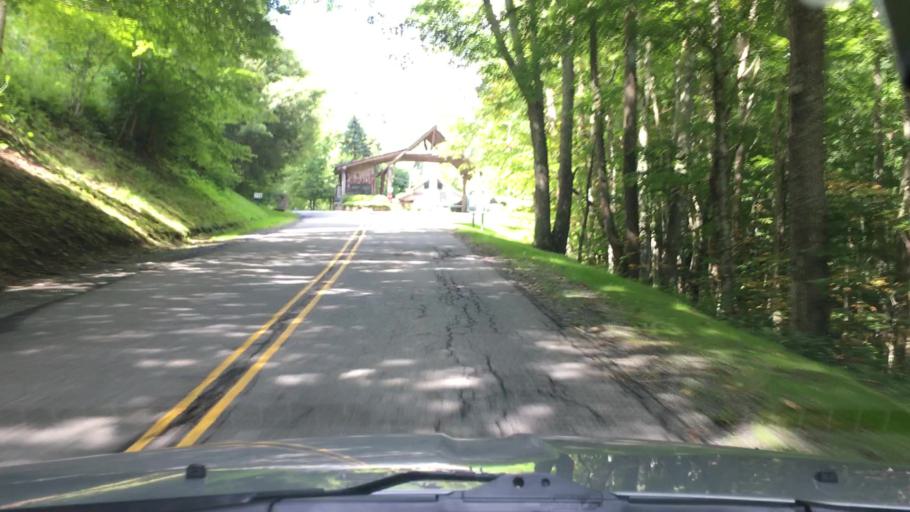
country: US
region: North Carolina
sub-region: Madison County
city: Mars Hill
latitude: 35.9528
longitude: -82.5169
